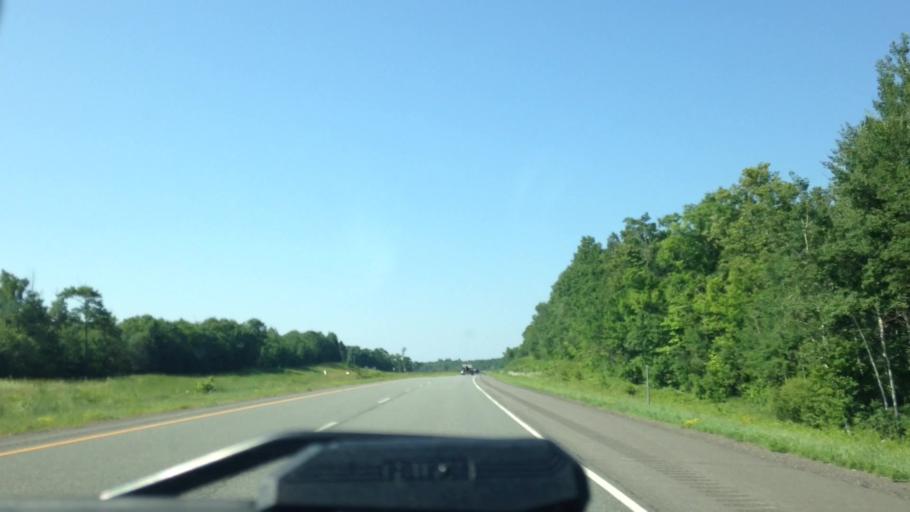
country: US
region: Wisconsin
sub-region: Douglas County
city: Lake Nebagamon
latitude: 46.4082
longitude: -91.8124
